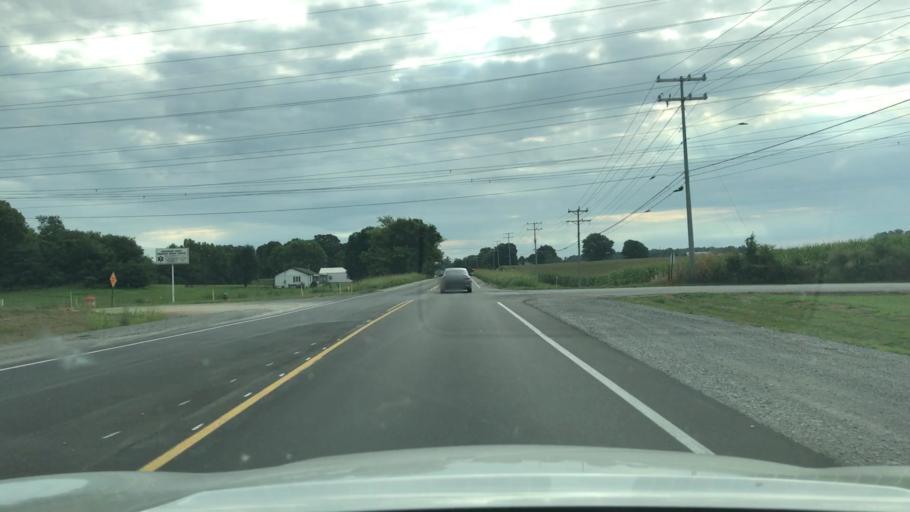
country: US
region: Kentucky
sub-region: Todd County
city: Guthrie
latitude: 36.6099
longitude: -87.2560
